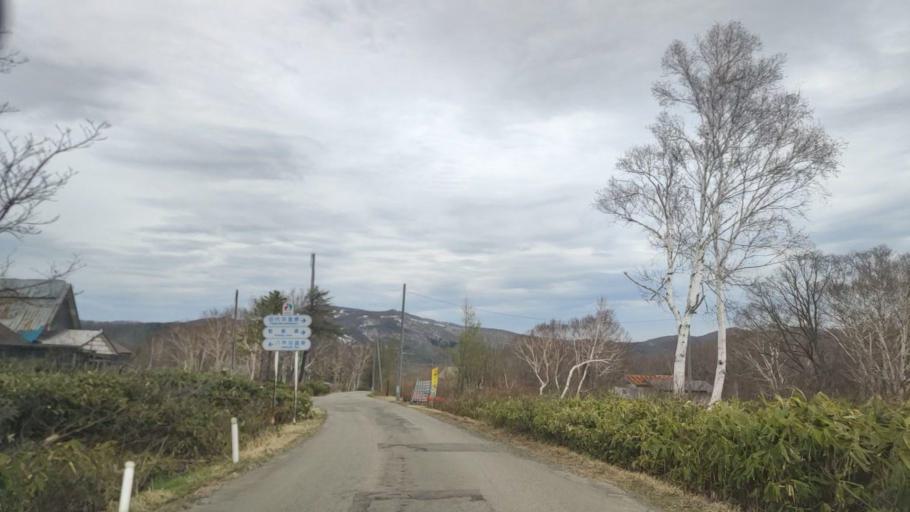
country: JP
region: Aomori
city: Aomori Shi
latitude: 40.6955
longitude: 140.9125
